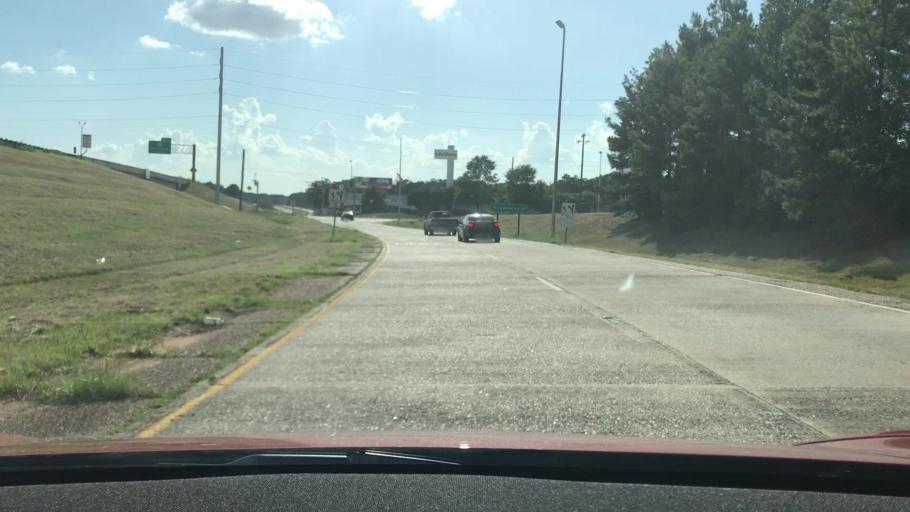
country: US
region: Louisiana
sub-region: Bossier Parish
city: Bossier City
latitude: 32.4211
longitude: -93.7615
